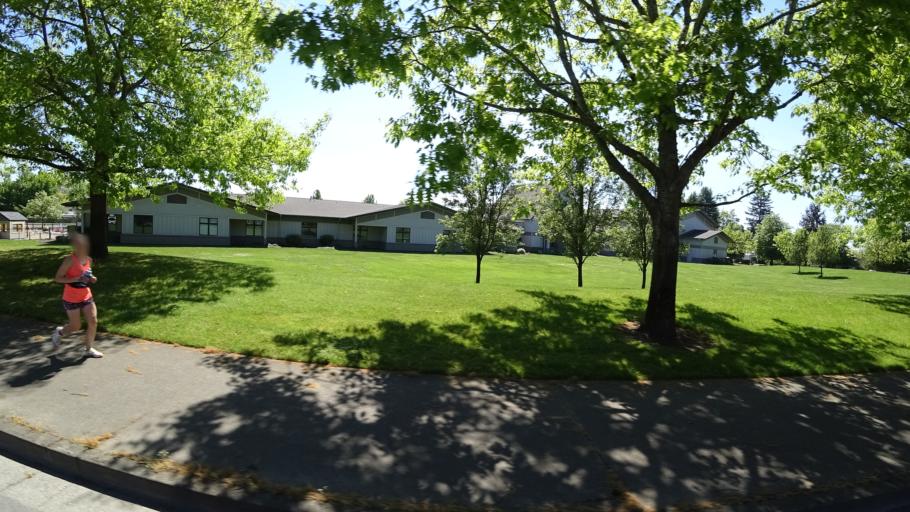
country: US
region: Oregon
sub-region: Washington County
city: Hillsboro
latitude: 45.5041
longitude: -122.9621
